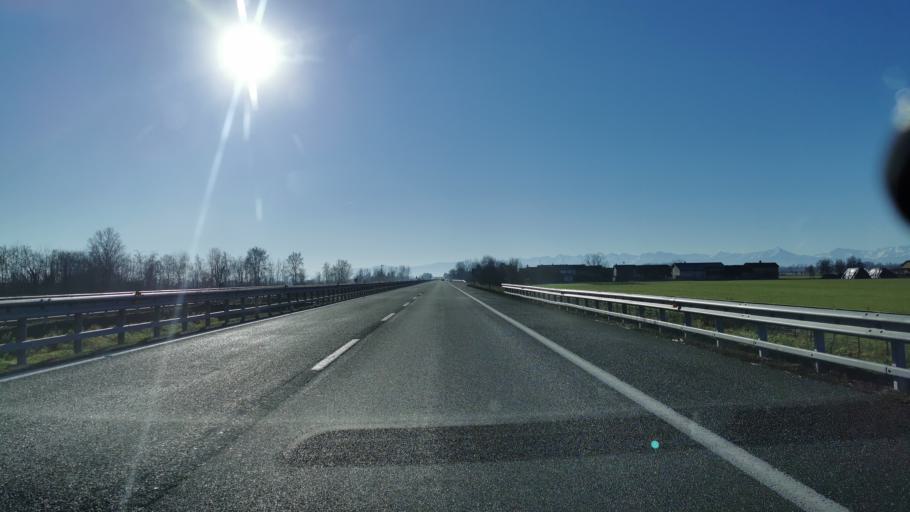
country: IT
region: Piedmont
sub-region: Provincia di Cuneo
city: Sanfre
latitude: 44.7155
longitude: 7.7597
